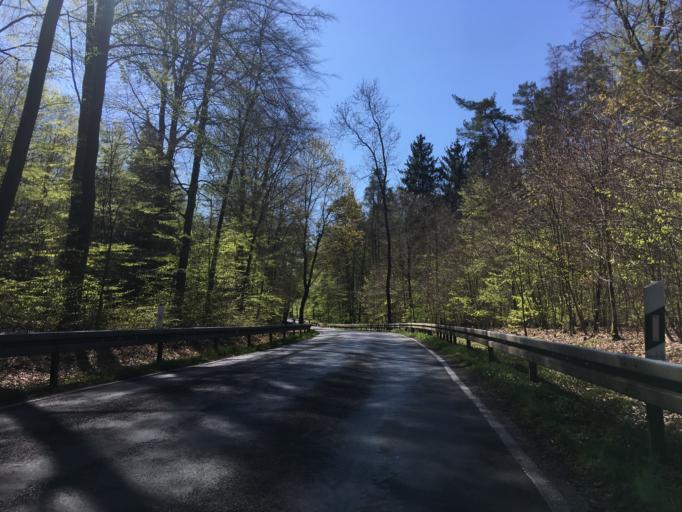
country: DE
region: Brandenburg
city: Bernau bei Berlin
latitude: 52.7265
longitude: 13.5670
